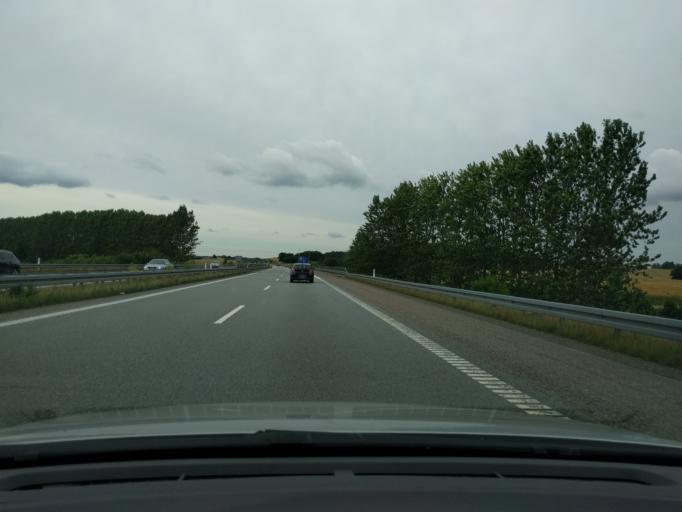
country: DK
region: South Denmark
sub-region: Vejle Kommune
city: Give
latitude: 55.8584
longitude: 9.2639
